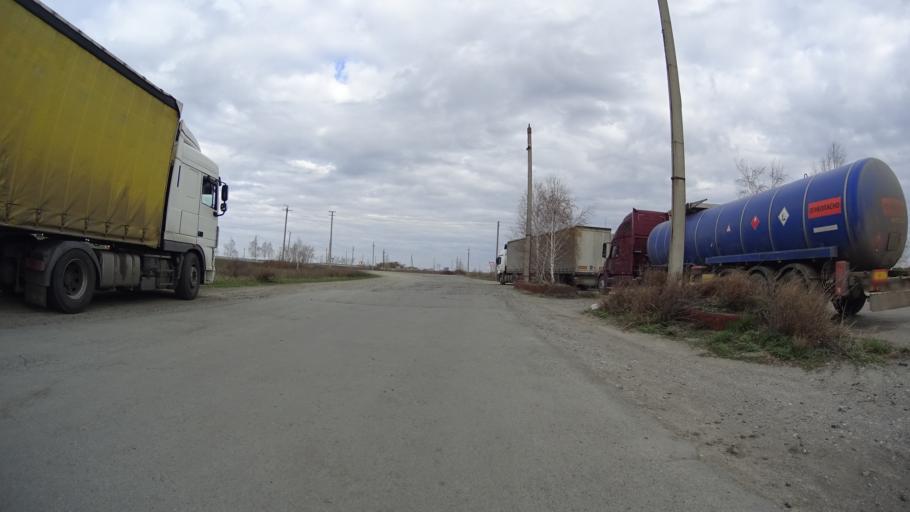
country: RU
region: Chelyabinsk
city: Troitsk
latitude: 54.0909
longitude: 61.4884
